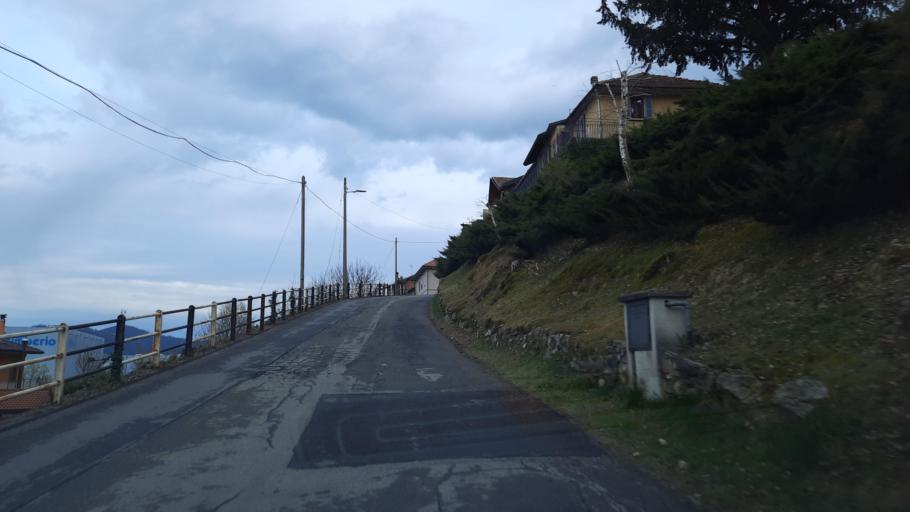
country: IT
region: Piedmont
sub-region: Provincia di Novara
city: San Maurizio D'Opaglio
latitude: 45.7713
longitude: 8.3912
